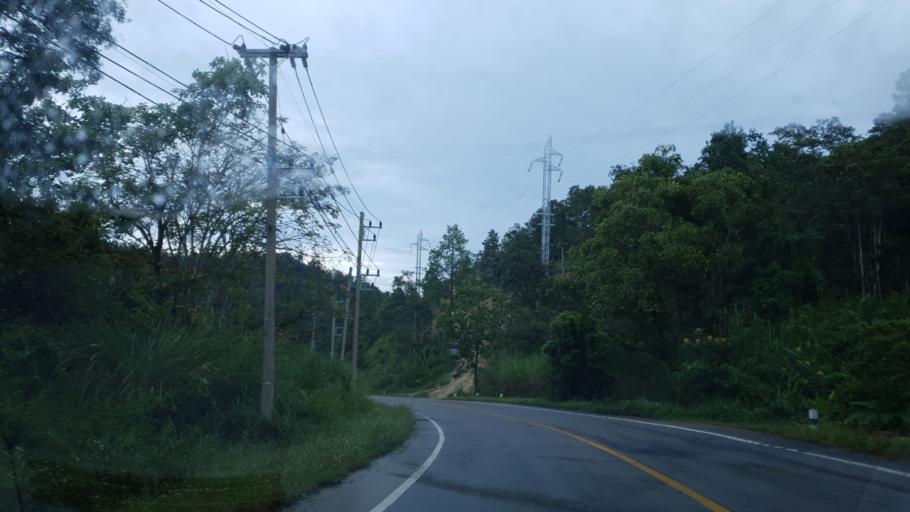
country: TH
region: Mae Hong Son
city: Ban Huai I Huak
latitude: 18.1375
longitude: 98.1918
